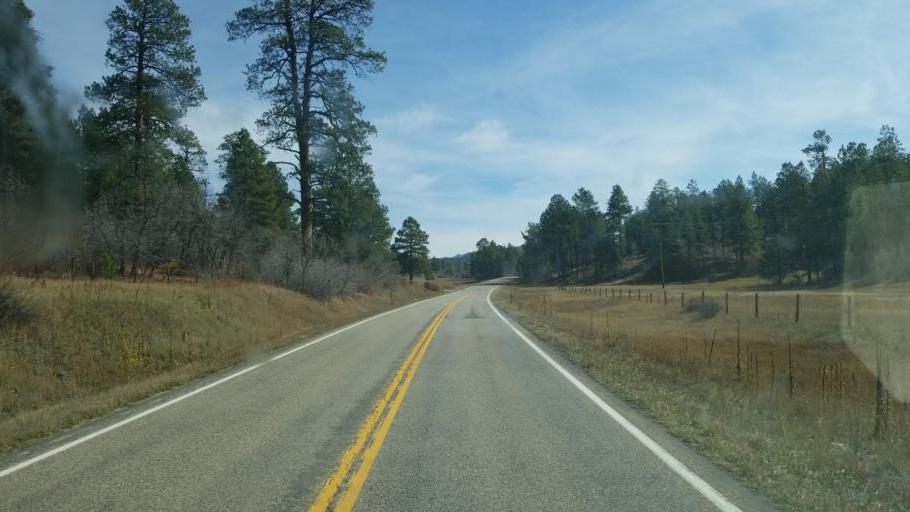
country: US
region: New Mexico
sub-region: Rio Arriba County
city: Dulce
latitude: 37.0751
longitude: -106.8409
